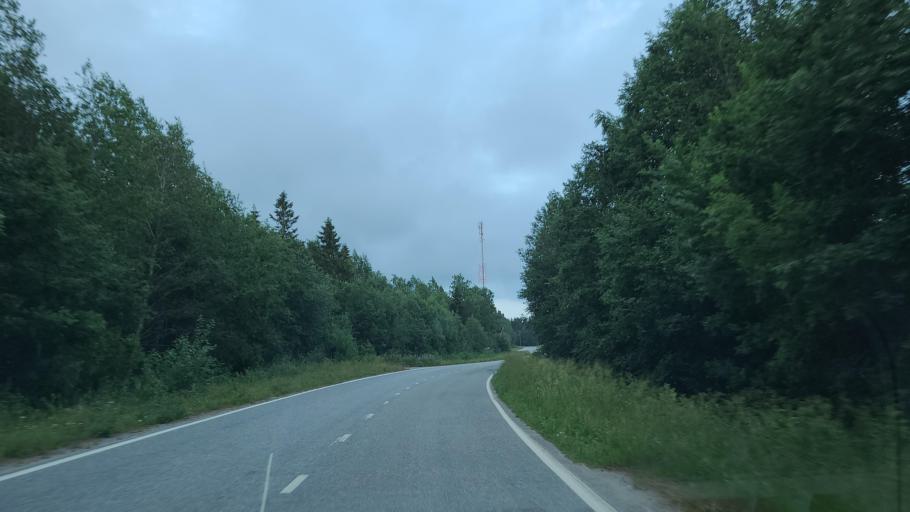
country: FI
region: Ostrobothnia
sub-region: Vaasa
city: Replot
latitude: 63.2893
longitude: 21.1138
